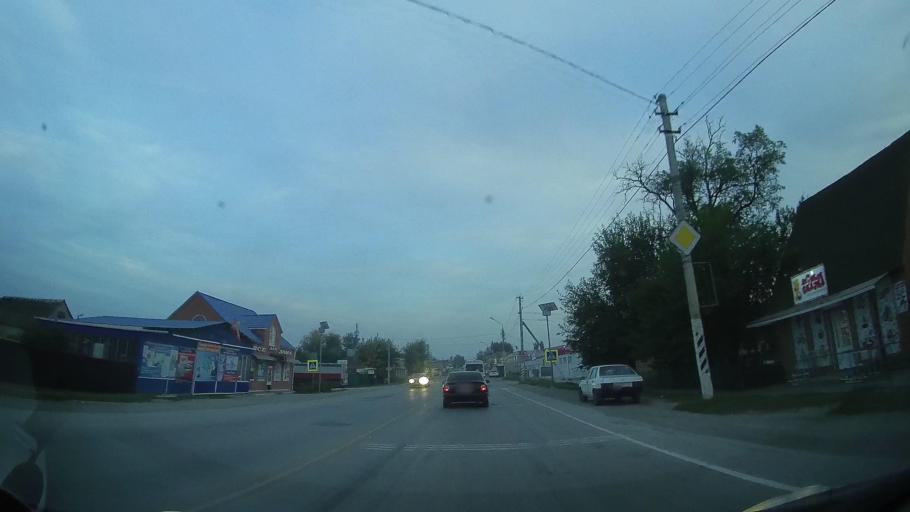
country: RU
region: Rostov
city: Kagal'nitskaya
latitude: 46.8836
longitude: 40.1468
